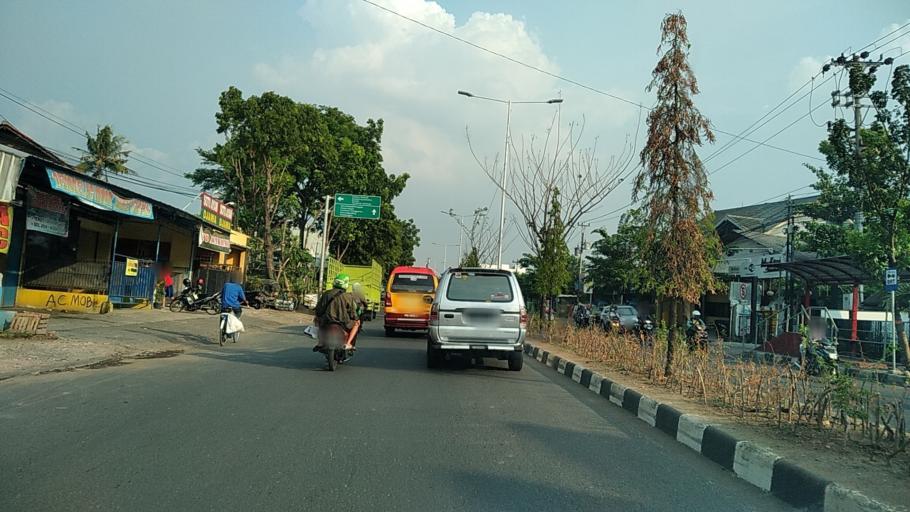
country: ID
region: Central Java
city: Semarang
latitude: -7.0045
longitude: 110.4694
